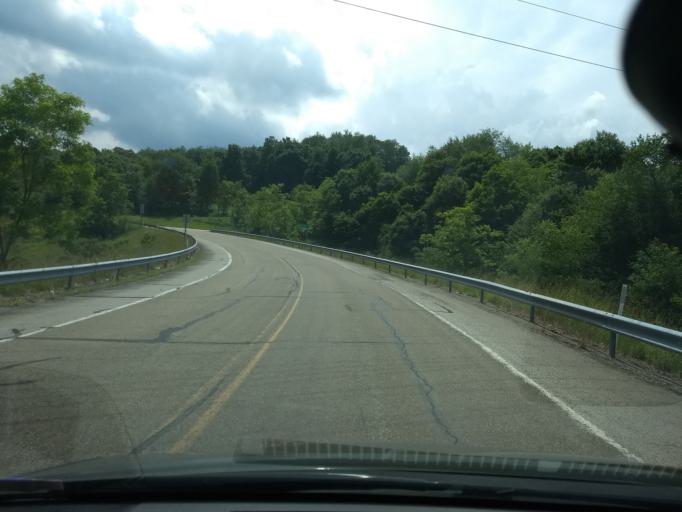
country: US
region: Pennsylvania
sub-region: Westmoreland County
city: Avonmore
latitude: 40.5204
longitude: -79.5018
